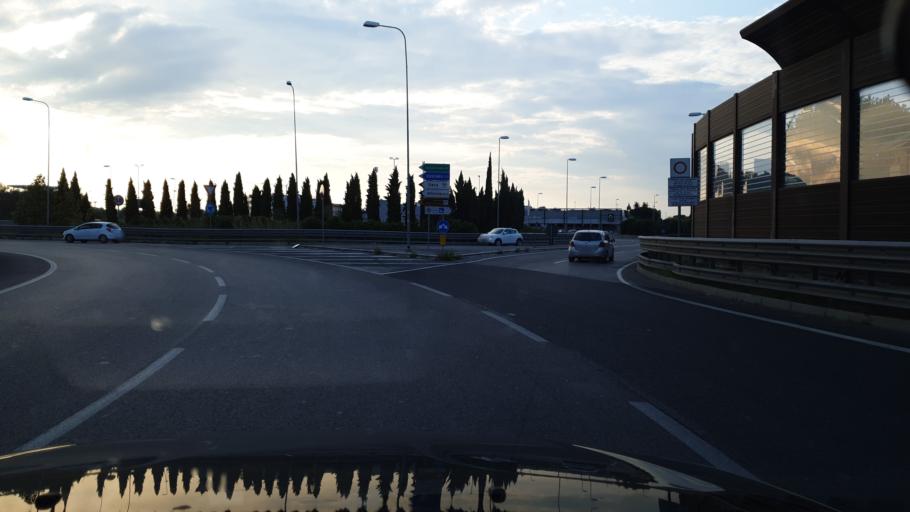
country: IT
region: Emilia-Romagna
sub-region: Provincia di Rimini
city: Rivazzurra
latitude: 44.0411
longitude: 12.5912
